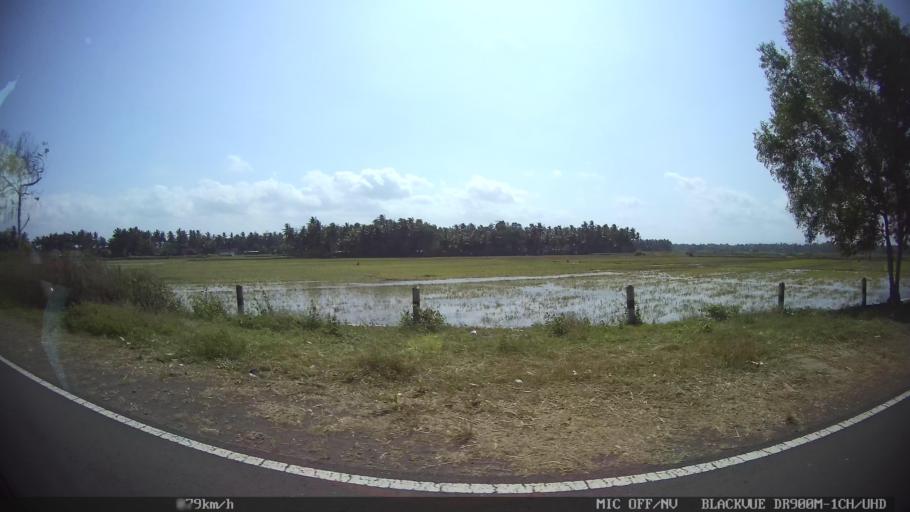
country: ID
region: Daerah Istimewa Yogyakarta
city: Srandakan
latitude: -7.9650
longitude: 110.2063
